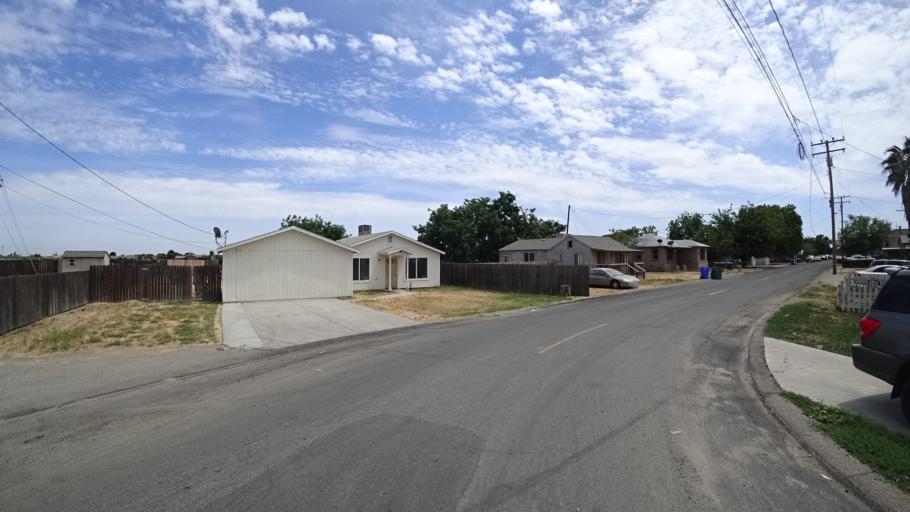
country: US
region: California
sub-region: Kings County
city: Armona
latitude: 36.3192
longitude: -119.7066
